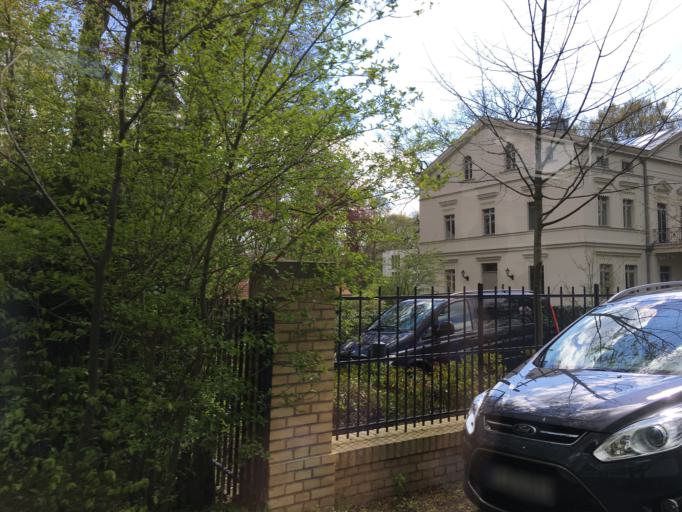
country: DE
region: Brandenburg
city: Potsdam
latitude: 52.4186
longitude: 13.0643
